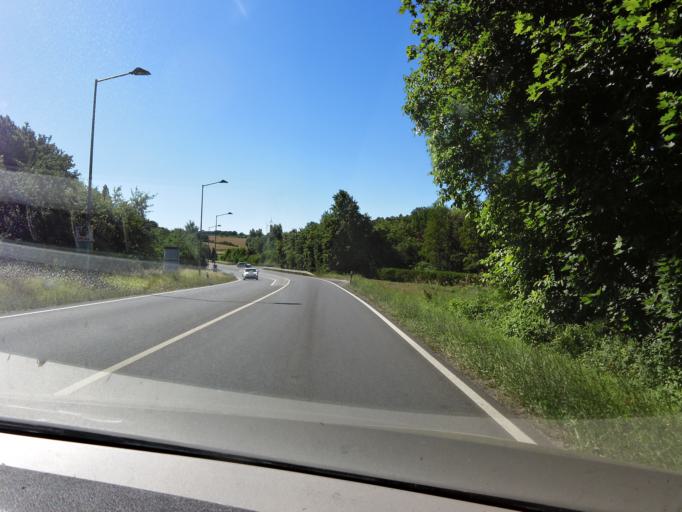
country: DE
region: Bavaria
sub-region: Regierungsbezirk Unterfranken
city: Kitzingen
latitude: 49.7407
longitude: 10.1422
